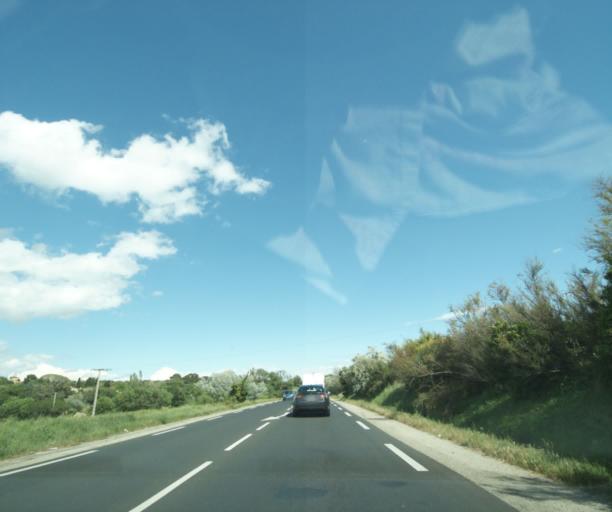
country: FR
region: Languedoc-Roussillon
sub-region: Departement de l'Herault
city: Saint-Jean-de-Vedas
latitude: 43.5857
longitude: 3.8407
